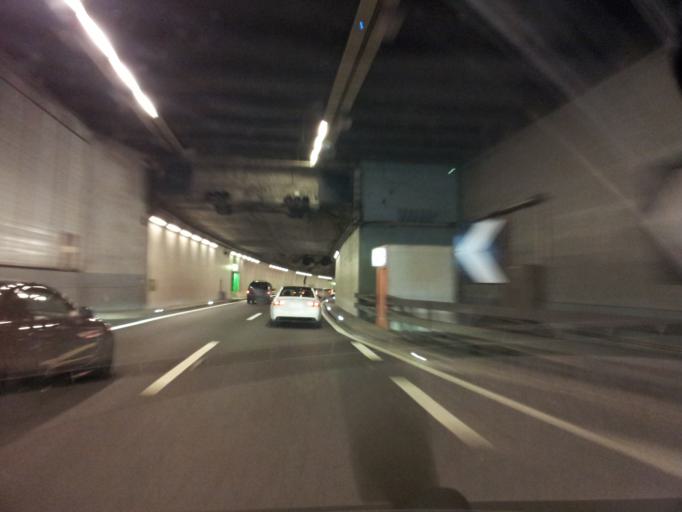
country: CH
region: Lucerne
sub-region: Lucerne-Stadt District
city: Luzern
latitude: 47.0391
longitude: 8.2941
